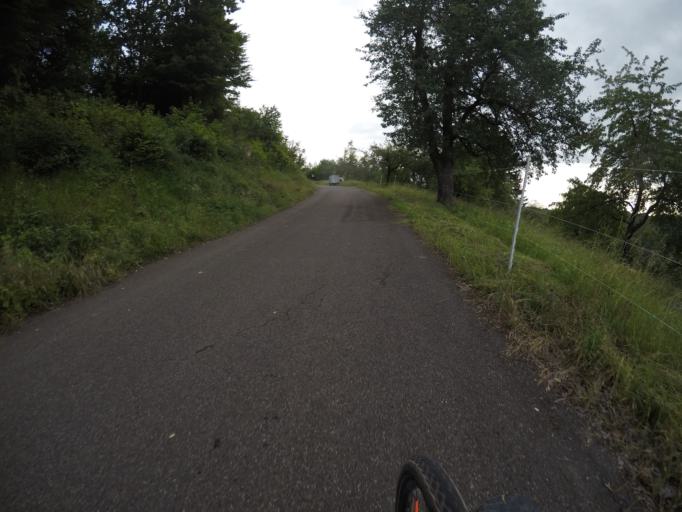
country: DE
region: Baden-Wuerttemberg
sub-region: Regierungsbezirk Stuttgart
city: Kohlberg
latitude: 48.5724
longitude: 9.3275
